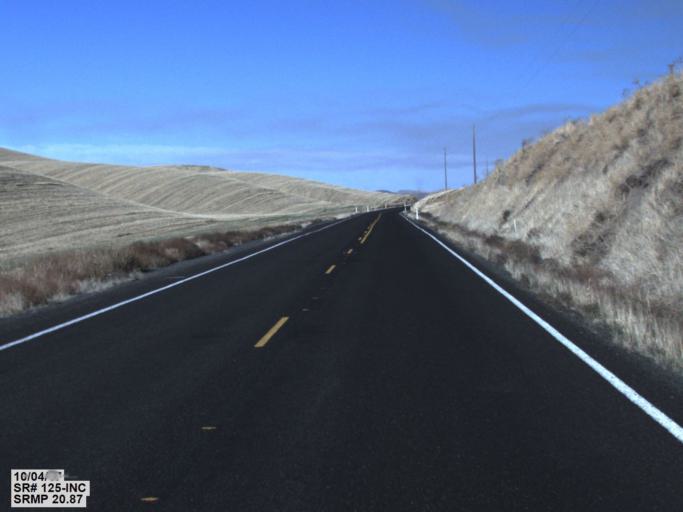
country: US
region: Washington
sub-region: Walla Walla County
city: Walla Walla
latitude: 46.2604
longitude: -118.3547
